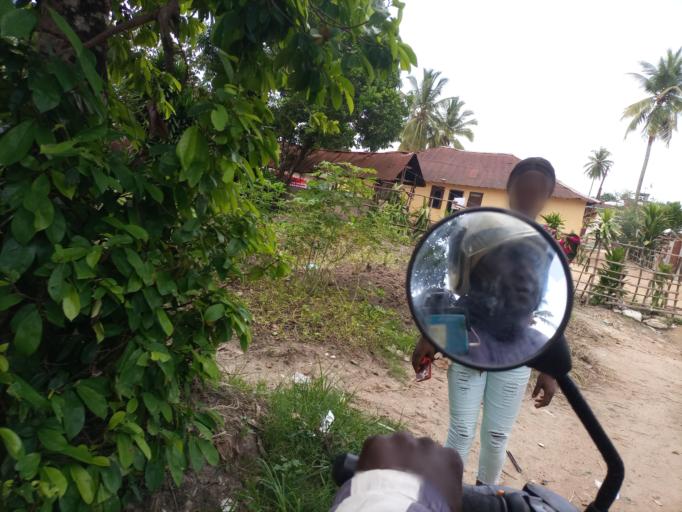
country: SL
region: Southern Province
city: Bo
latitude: 7.9547
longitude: -11.7354
